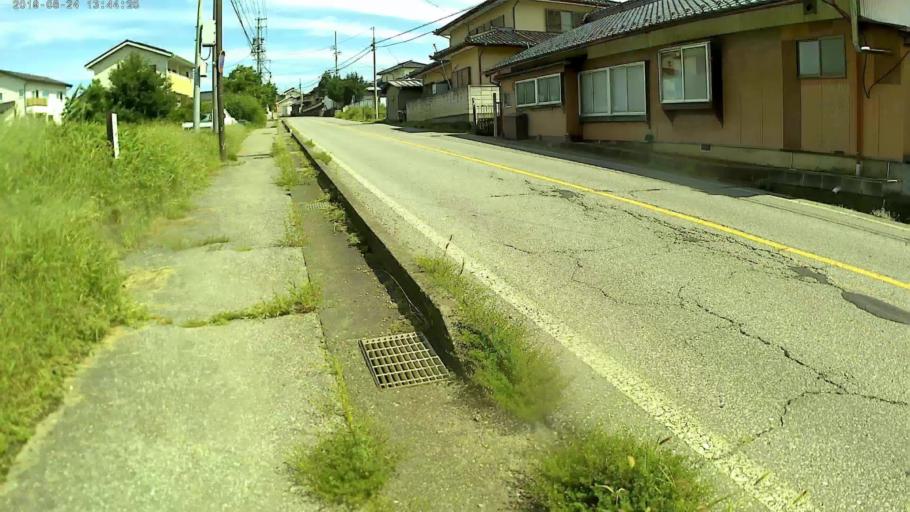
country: JP
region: Nagano
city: Komoro
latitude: 36.2752
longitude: 138.4023
